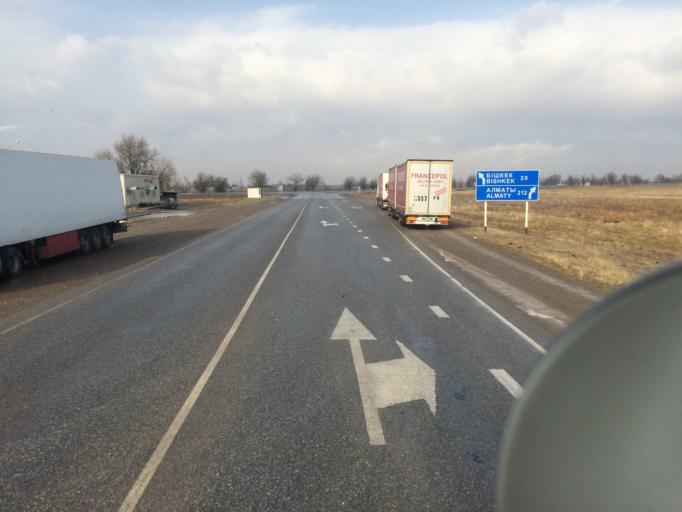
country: KZ
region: Zhambyl
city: Georgiyevka
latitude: 43.0875
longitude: 74.7081
